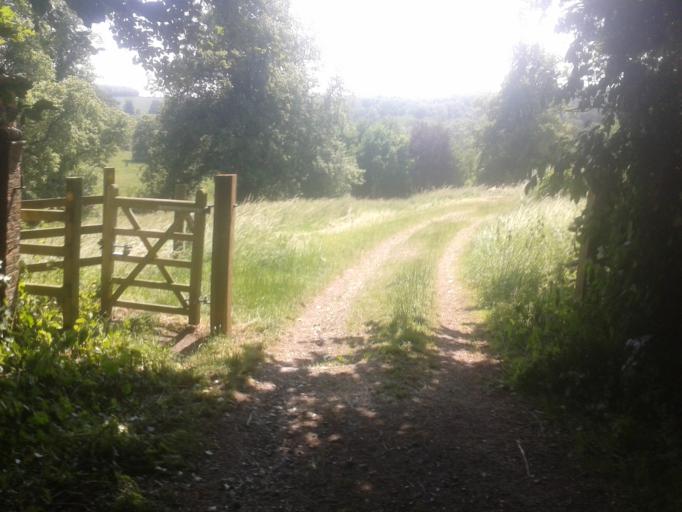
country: GB
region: England
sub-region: East Riding of Yorkshire
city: Londesborough
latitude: 53.8978
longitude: -0.6763
